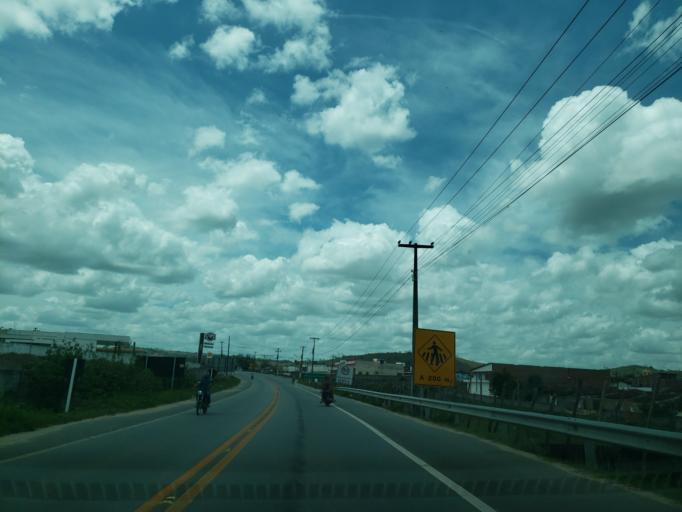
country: BR
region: Alagoas
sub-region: Uniao Dos Palmares
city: Uniao dos Palmares
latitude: -9.1531
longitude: -36.0129
